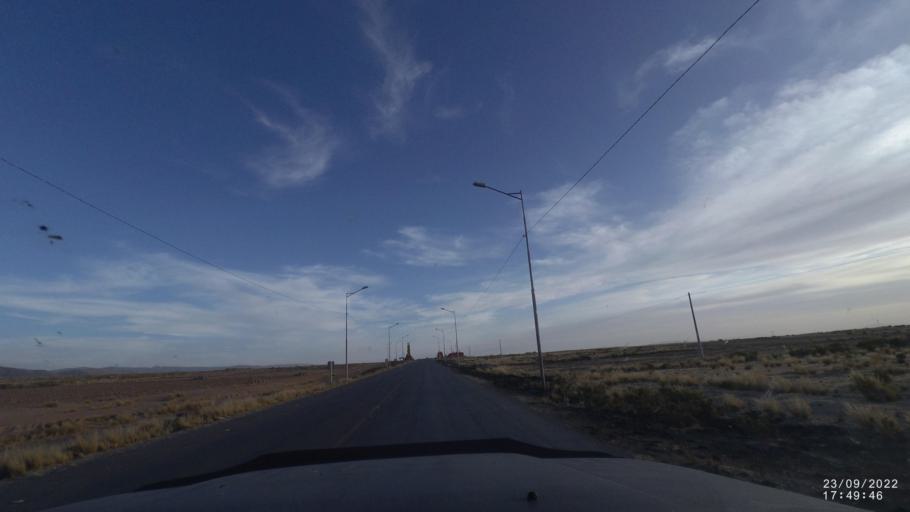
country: BO
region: Oruro
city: Challapata
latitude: -19.0239
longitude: -66.7766
